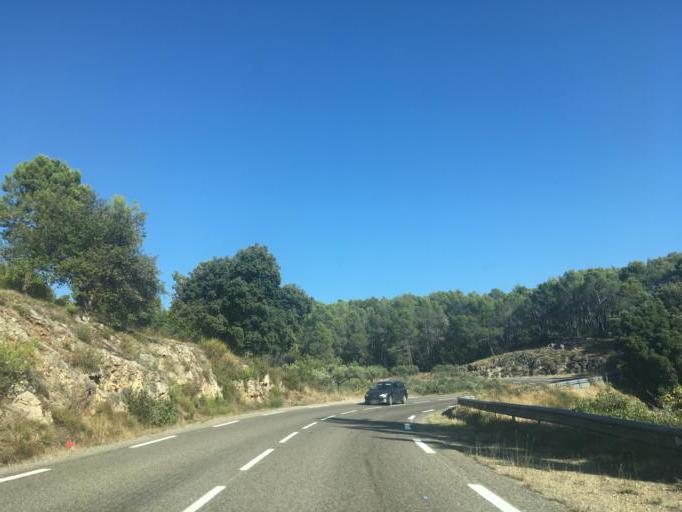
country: FR
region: Provence-Alpes-Cote d'Azur
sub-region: Departement du Var
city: Salernes
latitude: 43.5765
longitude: 6.2218
